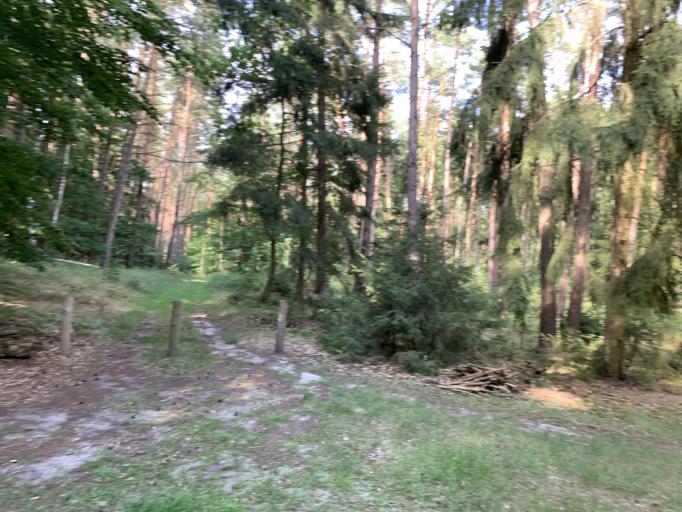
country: DE
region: Mecklenburg-Vorpommern
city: Carpin
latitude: 53.3487
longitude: 13.2284
